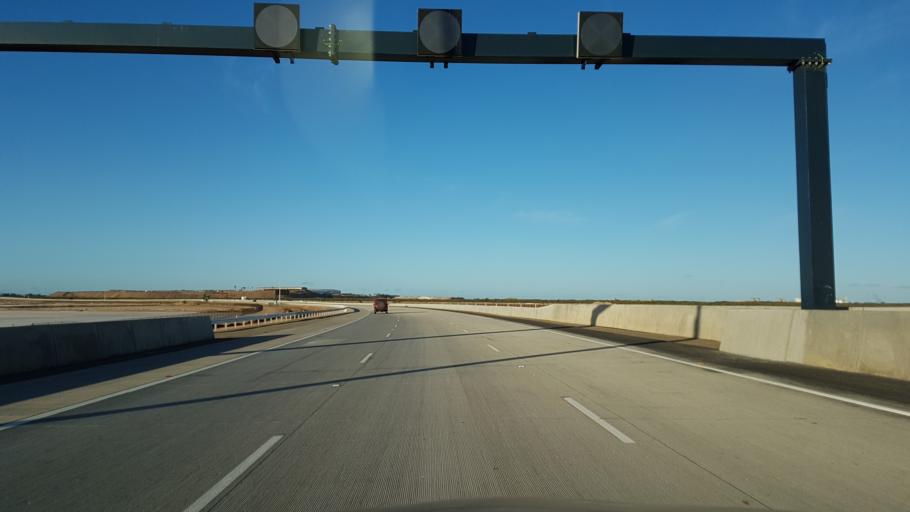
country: AU
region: South Australia
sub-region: Port Adelaide Enfield
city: Enfield
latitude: -34.8111
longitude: 138.5649
